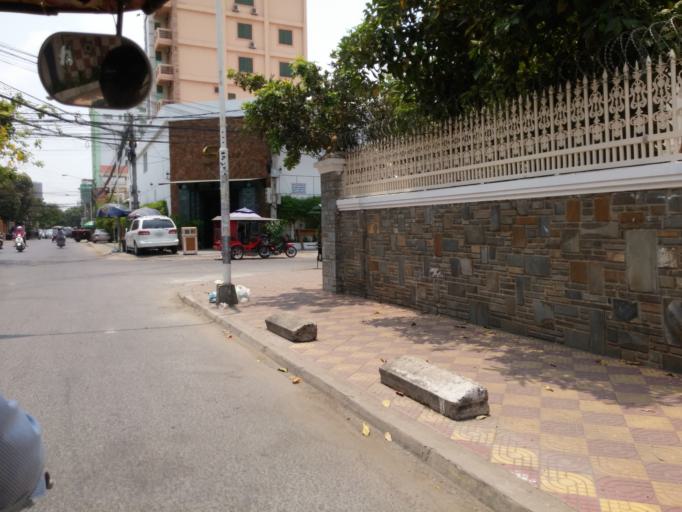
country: KH
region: Phnom Penh
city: Phnom Penh
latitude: 11.5584
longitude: 104.9191
